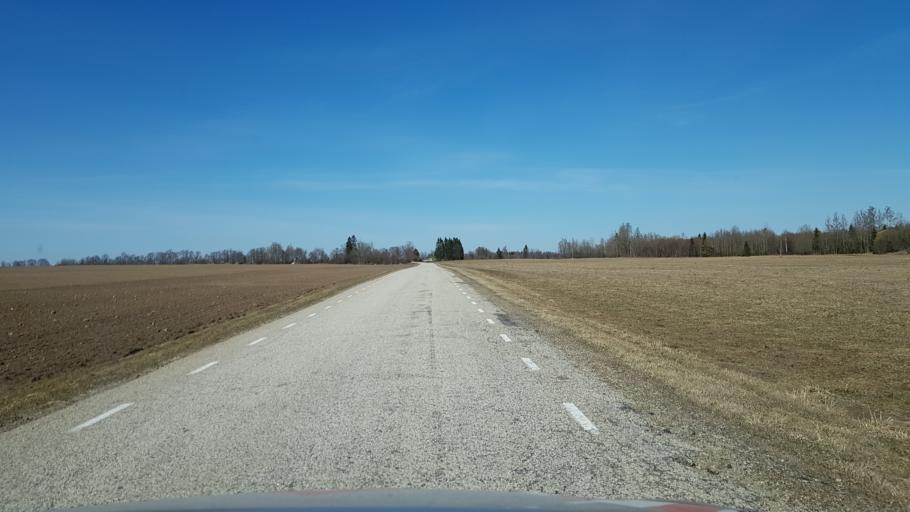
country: EE
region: Laeaene-Virumaa
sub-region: Vinni vald
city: Vinni
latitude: 59.0818
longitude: 26.5461
